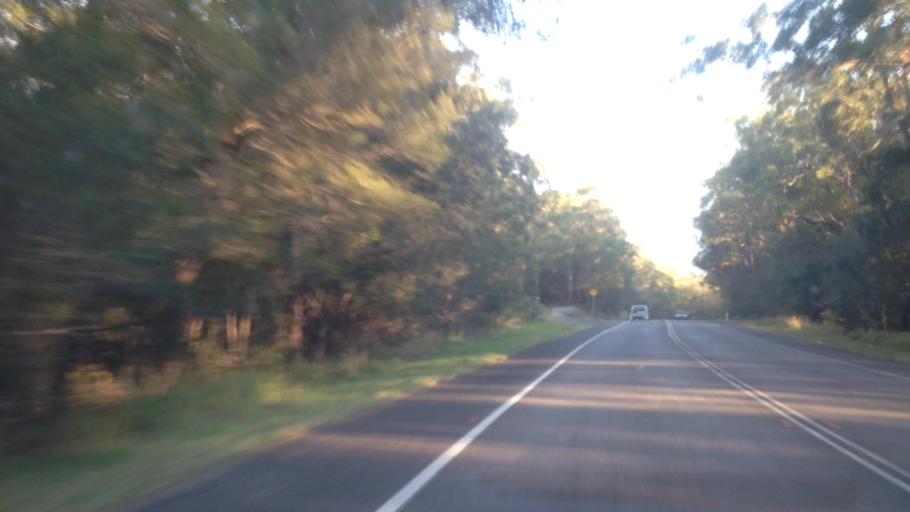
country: AU
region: New South Wales
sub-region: Lake Macquarie Shire
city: Cooranbong
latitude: -33.0558
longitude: 151.4742
